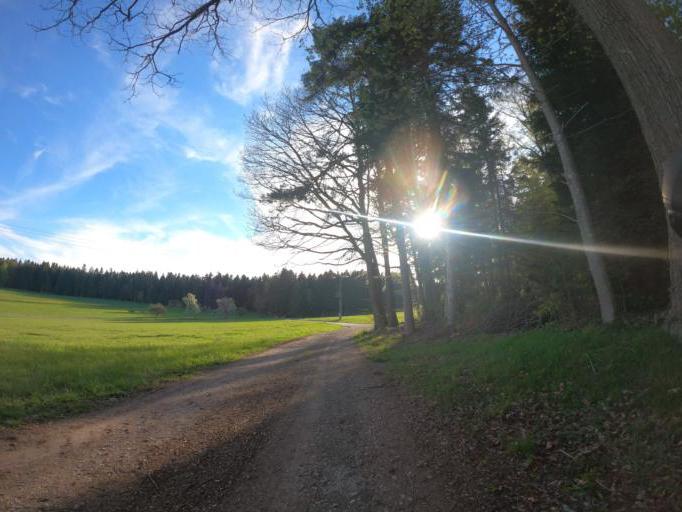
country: DE
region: Baden-Wuerttemberg
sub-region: Karlsruhe Region
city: Oberreichenbach
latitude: 48.7117
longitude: 8.6560
